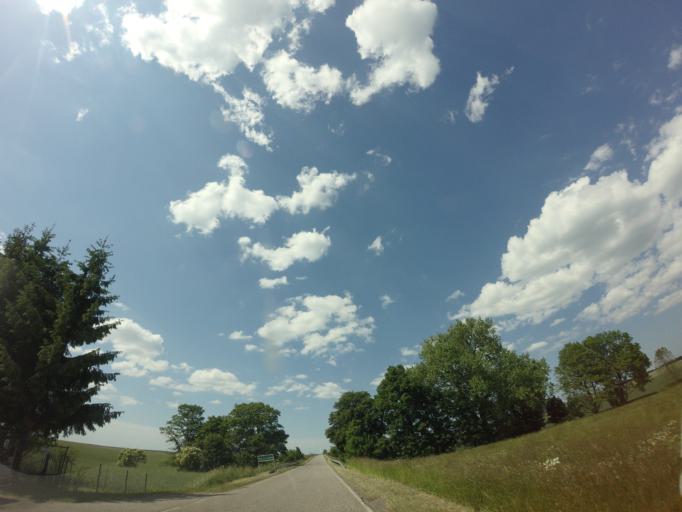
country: PL
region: West Pomeranian Voivodeship
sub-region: Powiat stargardzki
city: Dolice
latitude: 53.1635
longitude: 15.2302
